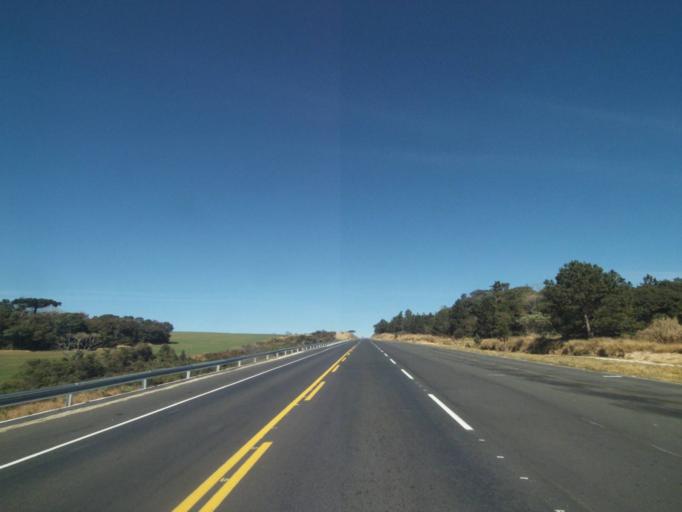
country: BR
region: Parana
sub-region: Tibagi
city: Tibagi
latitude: -24.7931
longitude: -50.4661
